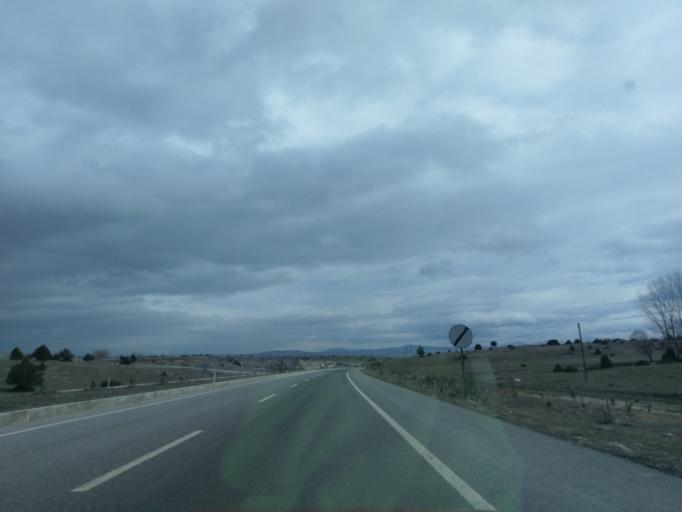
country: TR
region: Kuetahya
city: Aslanapa
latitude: 39.2308
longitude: 29.7701
